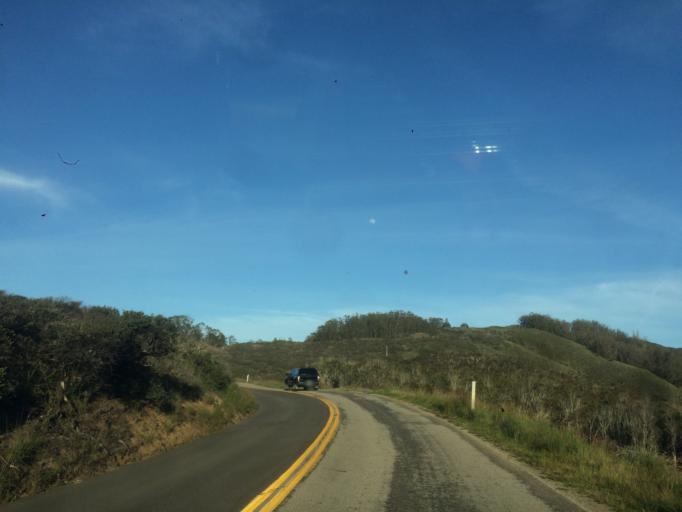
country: US
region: California
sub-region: San Luis Obispo County
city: Los Osos
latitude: 35.2982
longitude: -120.8666
